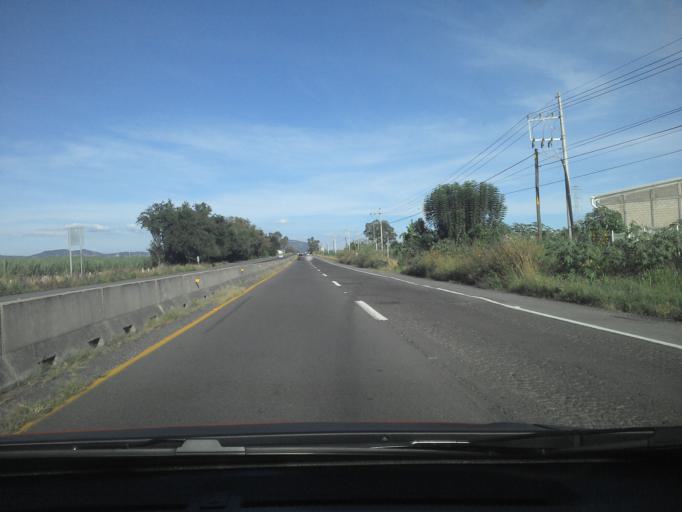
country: MX
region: Jalisco
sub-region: Tala
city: Los Ruisenores
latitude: 20.7073
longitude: -103.6766
